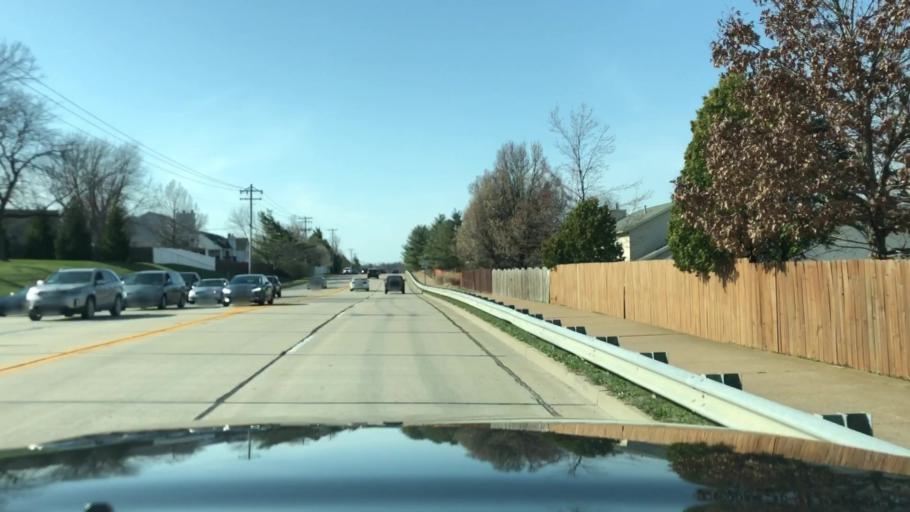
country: US
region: Missouri
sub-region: Saint Charles County
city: Saint Charles
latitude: 38.7730
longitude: -90.5503
